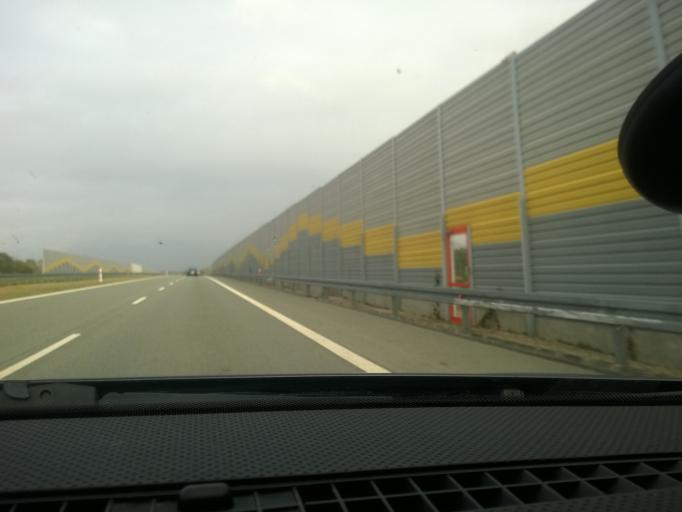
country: PL
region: Lodz Voivodeship
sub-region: Powiat pabianicki
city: Ksawerow
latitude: 51.6266
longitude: 19.3969
